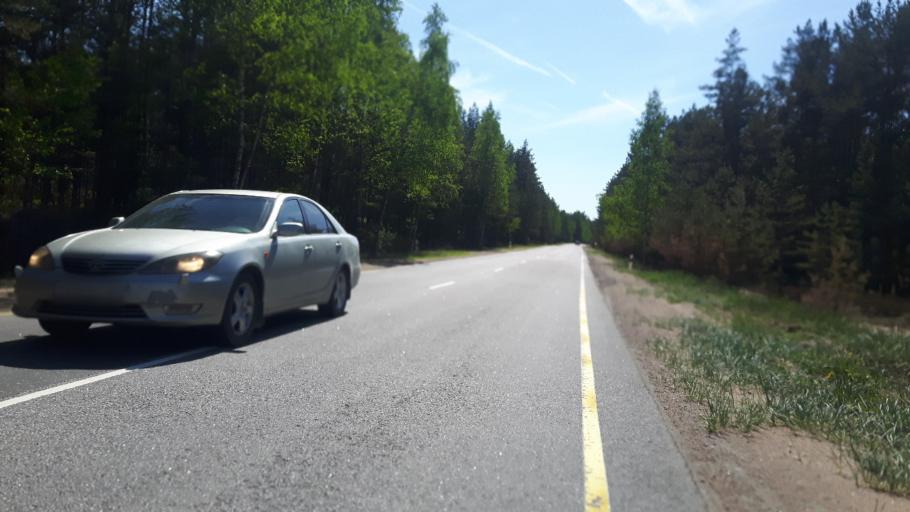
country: RU
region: Leningrad
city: Sista-Palkino
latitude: 59.7788
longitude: 28.8672
